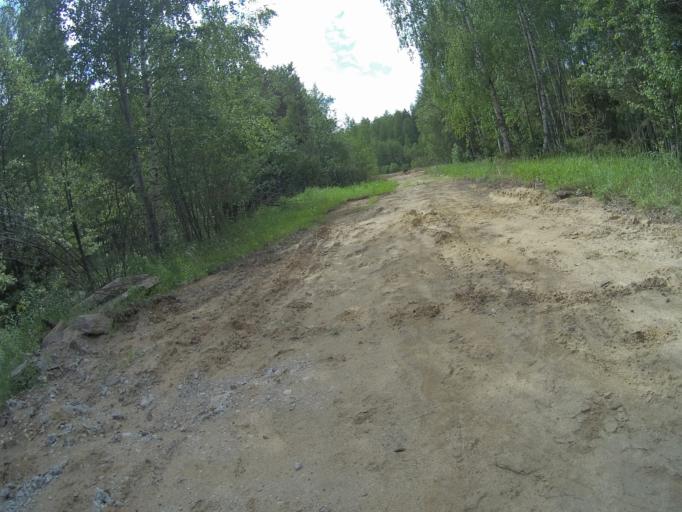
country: RU
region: Vladimir
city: Raduzhnyy
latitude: 55.9890
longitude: 40.2736
